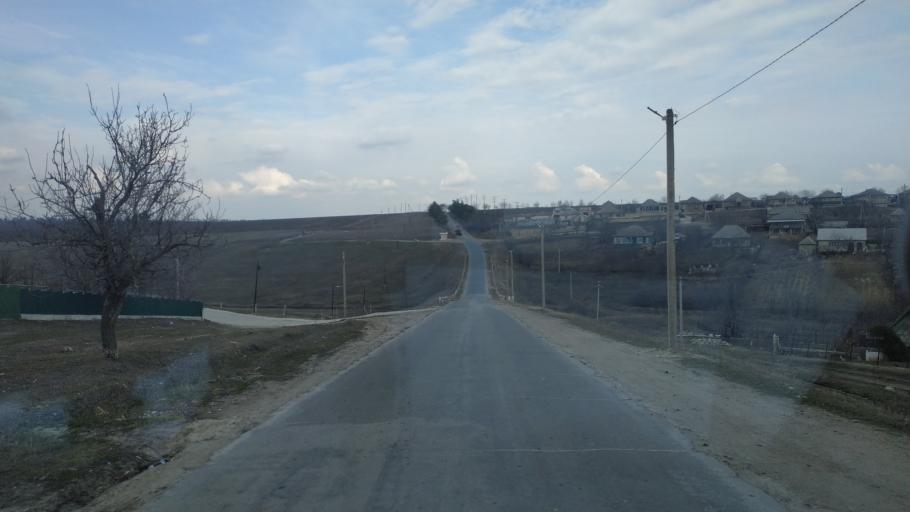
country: MD
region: Anenii Noi
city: Anenii Noi
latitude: 46.9047
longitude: 29.3204
